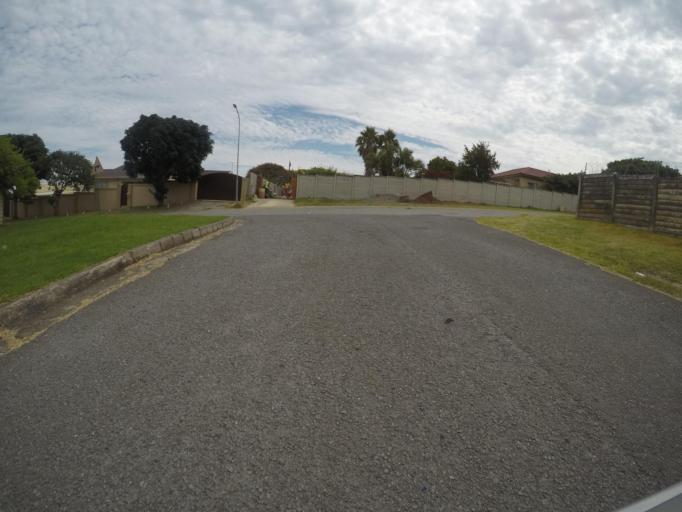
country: ZA
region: Eastern Cape
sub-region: Buffalo City Metropolitan Municipality
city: East London
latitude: -32.9967
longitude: 27.8707
